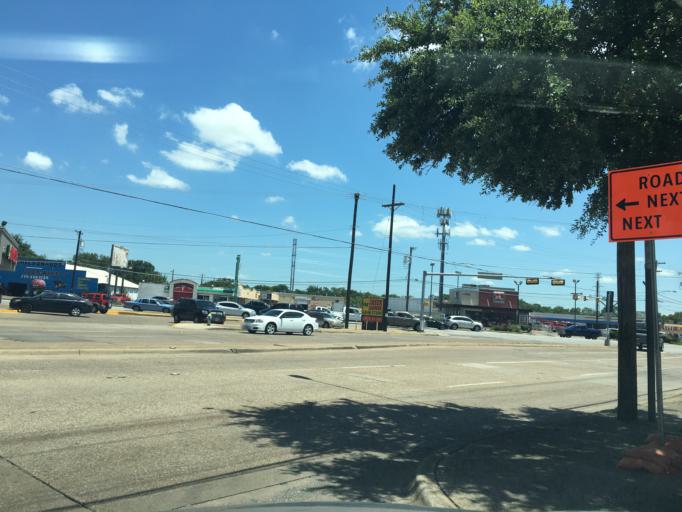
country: US
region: Texas
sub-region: Dallas County
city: Garland
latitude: 32.8502
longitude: -96.6834
